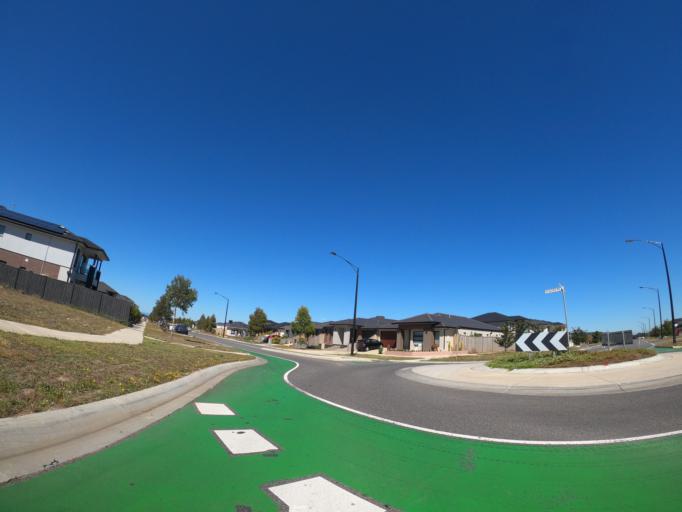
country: AU
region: Victoria
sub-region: Hume
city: Craigieburn
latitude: -37.5394
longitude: 144.8990
